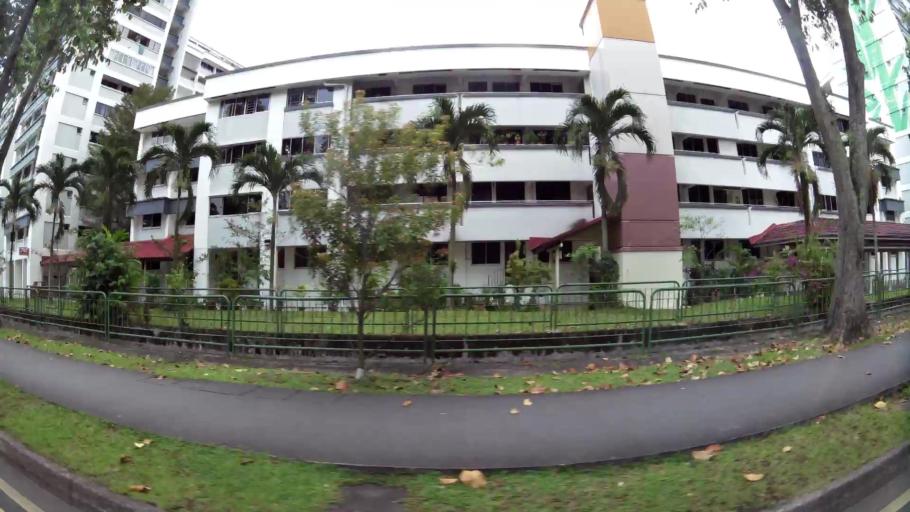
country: MY
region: Johor
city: Kampung Pasir Gudang Baru
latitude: 1.4204
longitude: 103.8317
